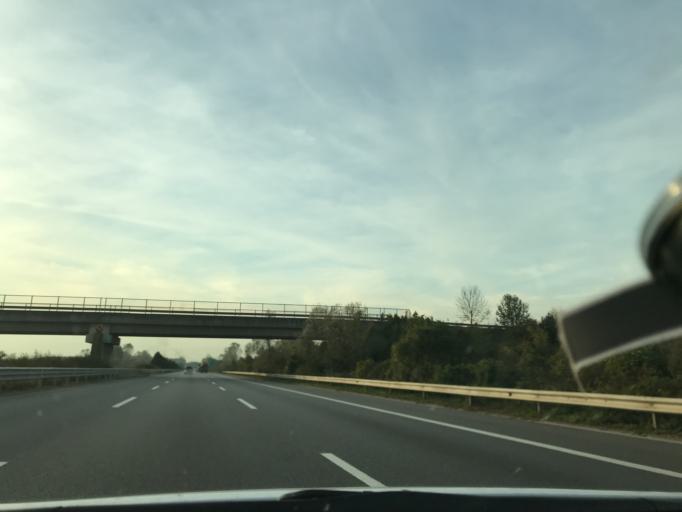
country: TR
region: Duzce
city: Cilimli
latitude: 40.8261
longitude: 31.0556
